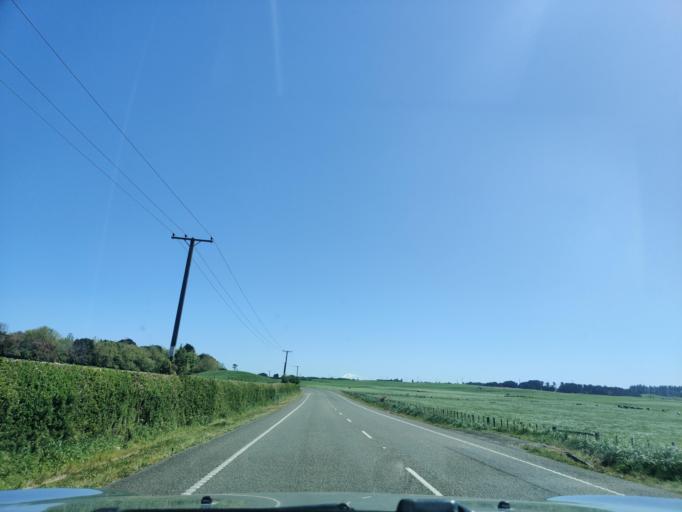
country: NZ
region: Taranaki
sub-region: South Taranaki District
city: Patea
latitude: -39.7798
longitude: 174.6913
